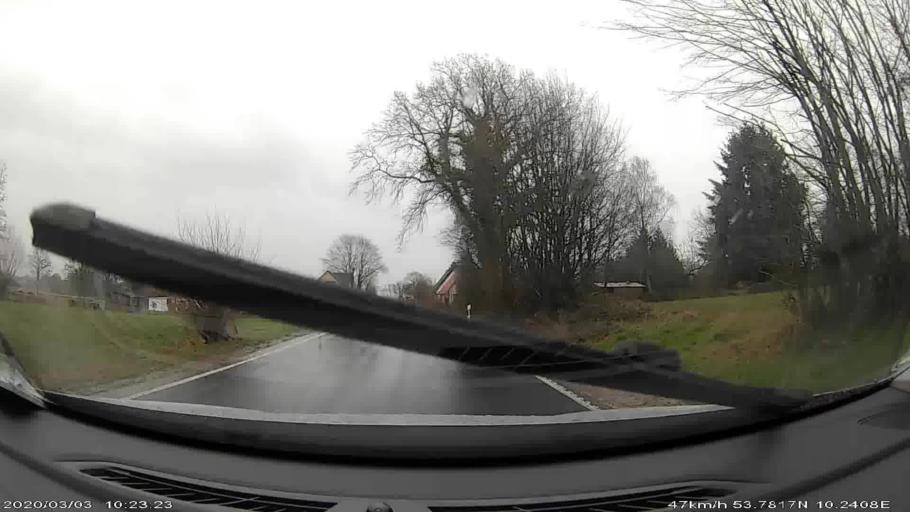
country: DE
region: Schleswig-Holstein
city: Sulfeld
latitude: 53.7808
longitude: 10.2413
